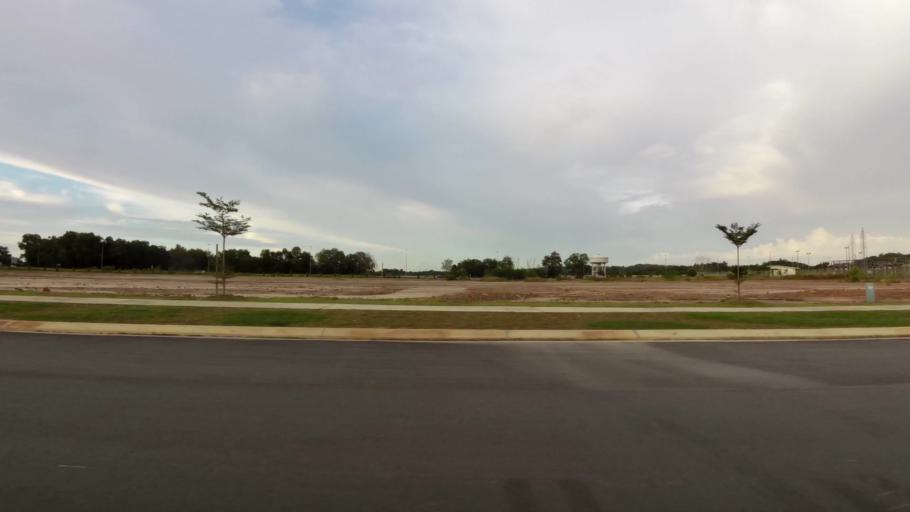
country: BN
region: Brunei and Muara
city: Bandar Seri Begawan
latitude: 4.9937
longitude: 114.9850
